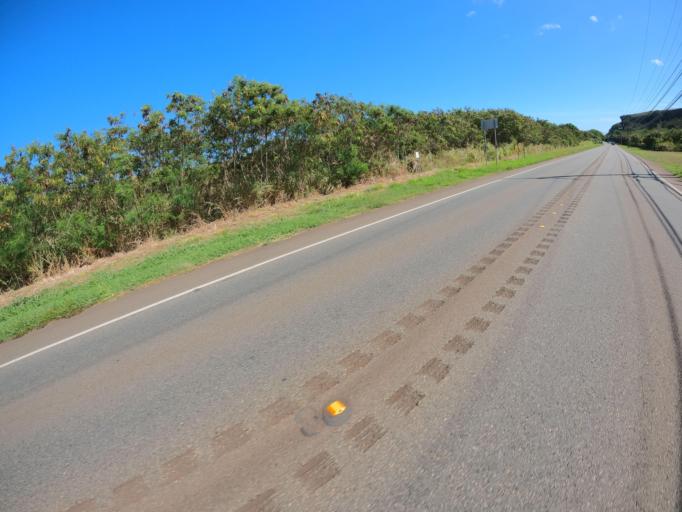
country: US
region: Hawaii
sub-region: Honolulu County
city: Kahuku
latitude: 21.6918
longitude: -157.9742
